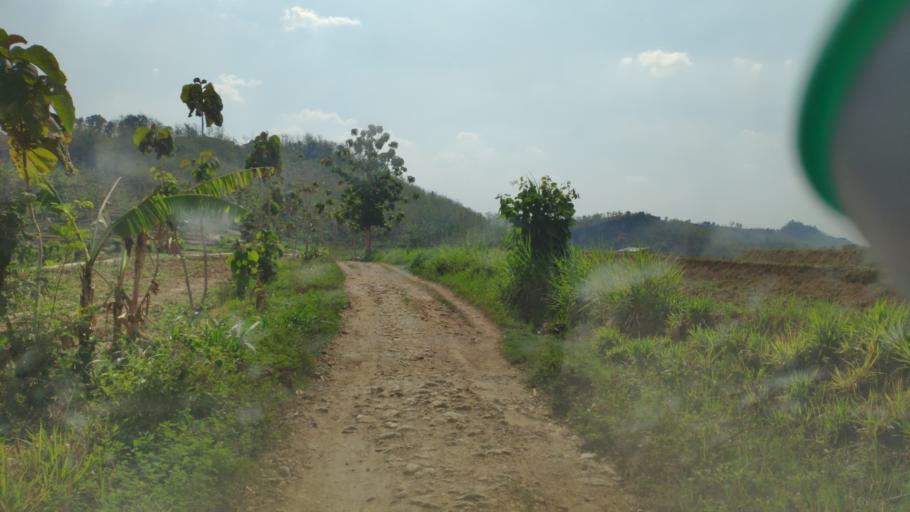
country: ID
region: Central Java
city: Ngapus
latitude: -6.9348
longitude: 111.2142
